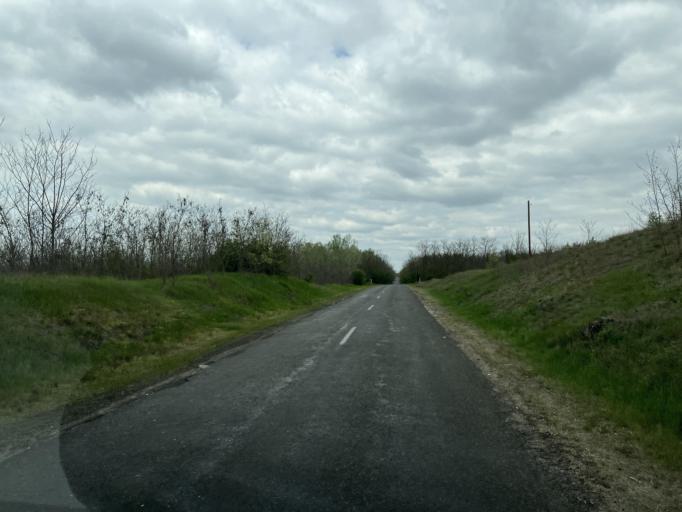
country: HU
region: Pest
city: Orkeny
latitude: 47.1088
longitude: 19.3597
